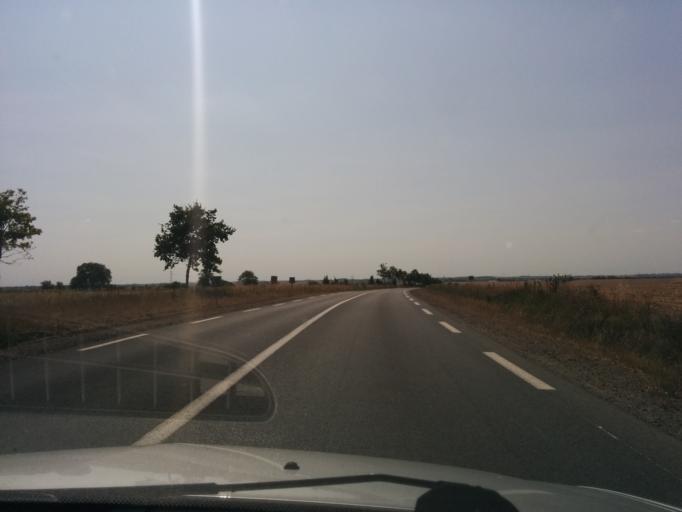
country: FR
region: Poitou-Charentes
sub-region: Departement de la Vienne
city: Jaunay-Clan
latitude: 46.6840
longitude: 0.3541
